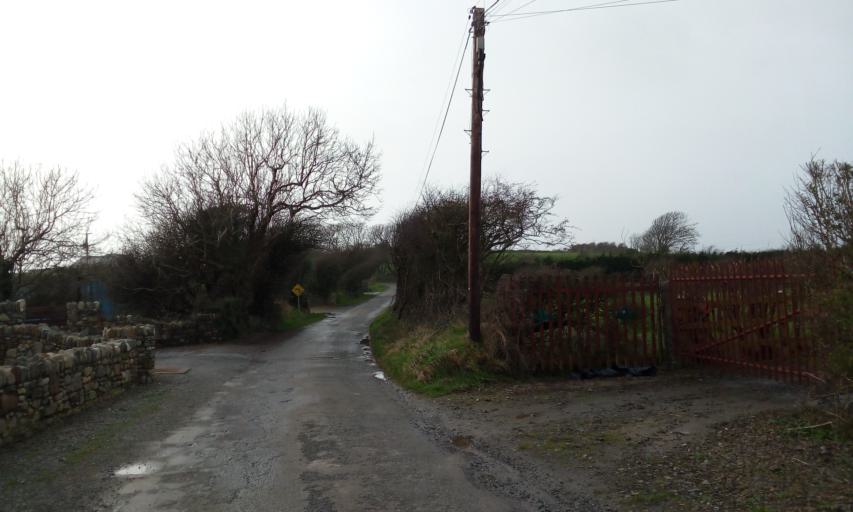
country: IE
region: Leinster
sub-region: Loch Garman
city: Loch Garman
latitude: 52.2215
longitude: -6.7085
